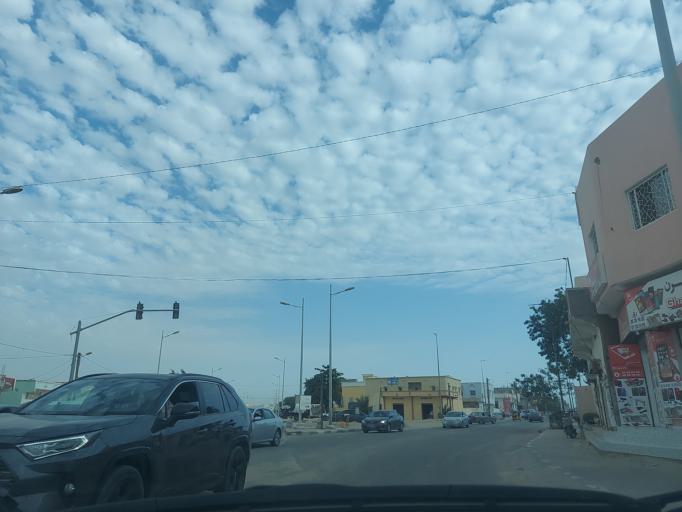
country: MR
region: Nouakchott
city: Nouakchott
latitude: 18.1176
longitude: -15.9749
